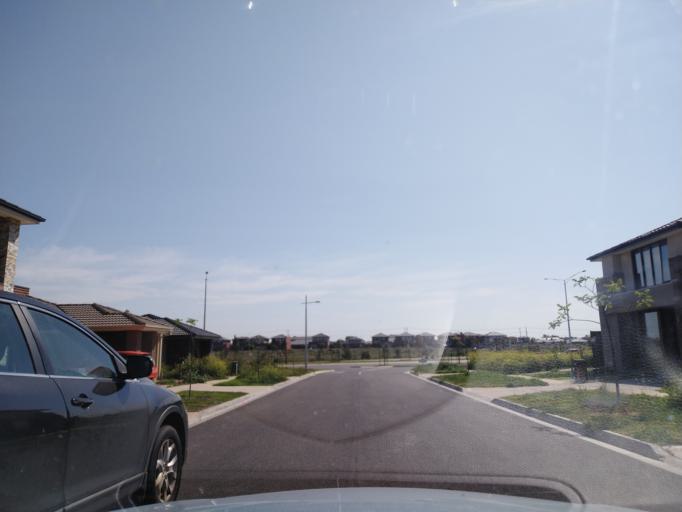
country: AU
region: Victoria
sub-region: Wyndham
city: Williams Landing
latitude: -37.8409
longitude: 144.7326
